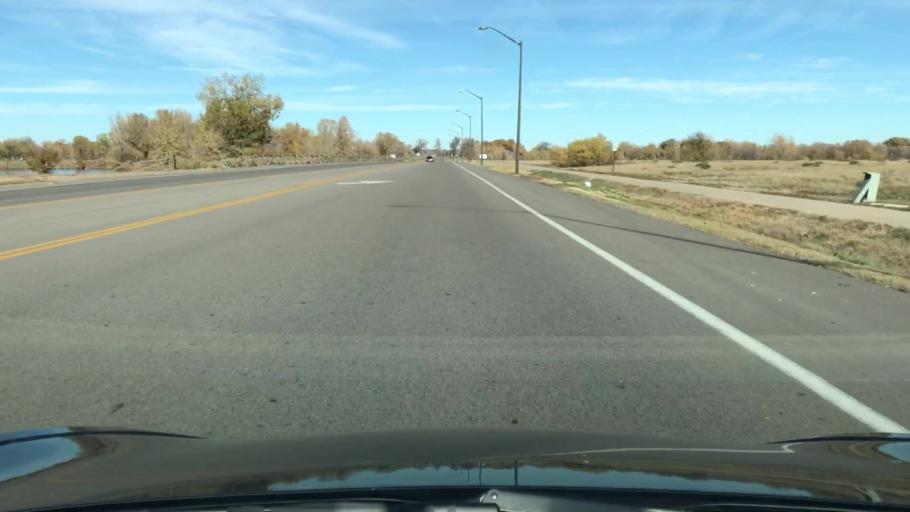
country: US
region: Colorado
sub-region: Larimer County
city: Fort Collins
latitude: 40.5698
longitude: -105.0392
